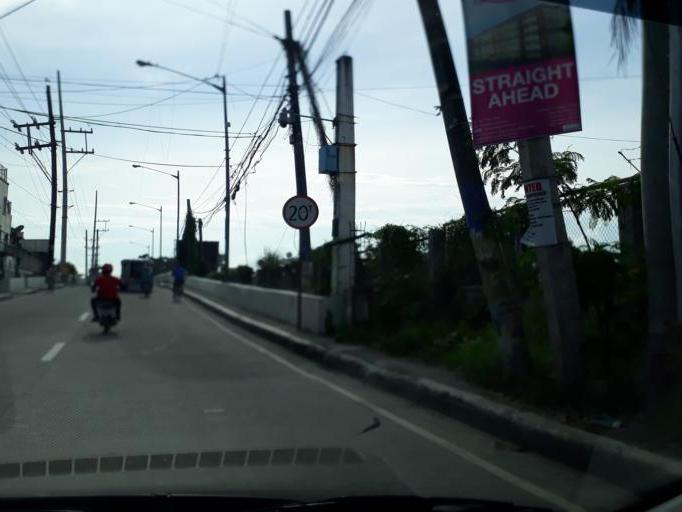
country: PH
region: Calabarzon
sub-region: Province of Rizal
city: Navotas
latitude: 14.6709
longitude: 120.9539
